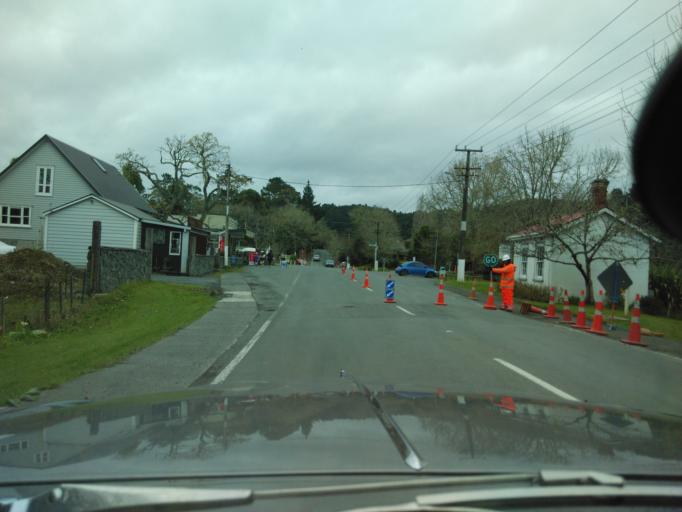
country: NZ
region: Auckland
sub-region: Auckland
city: Warkworth
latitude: -36.5127
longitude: 174.6615
